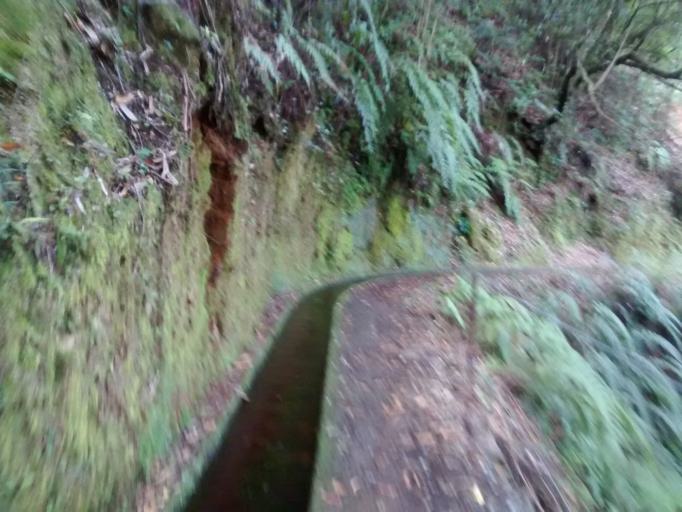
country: PT
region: Madeira
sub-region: Santana
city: Santana
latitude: 32.8076
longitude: -16.9383
